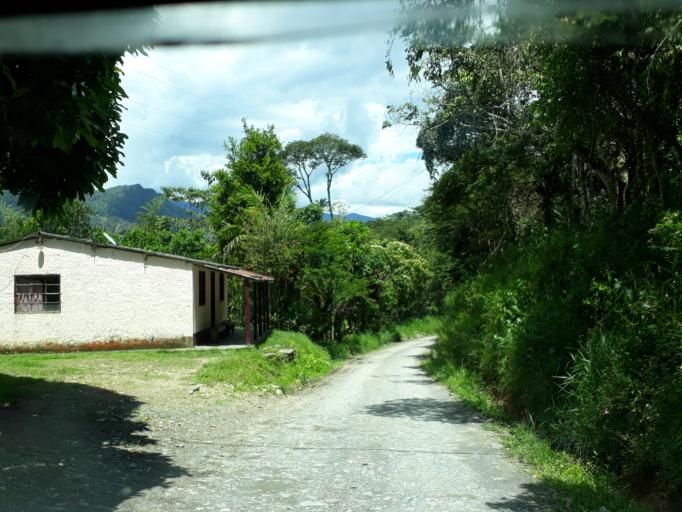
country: CO
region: Cundinamarca
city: Topaipi
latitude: 5.3712
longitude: -74.1971
